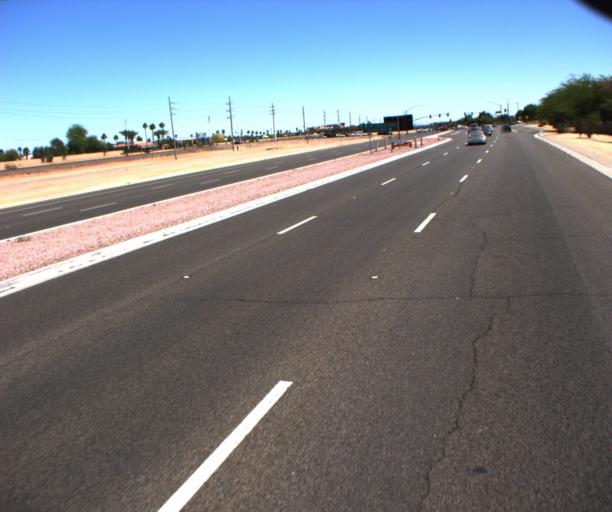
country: US
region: Arizona
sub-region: Maricopa County
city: Sun City West
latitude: 33.6713
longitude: -112.3928
